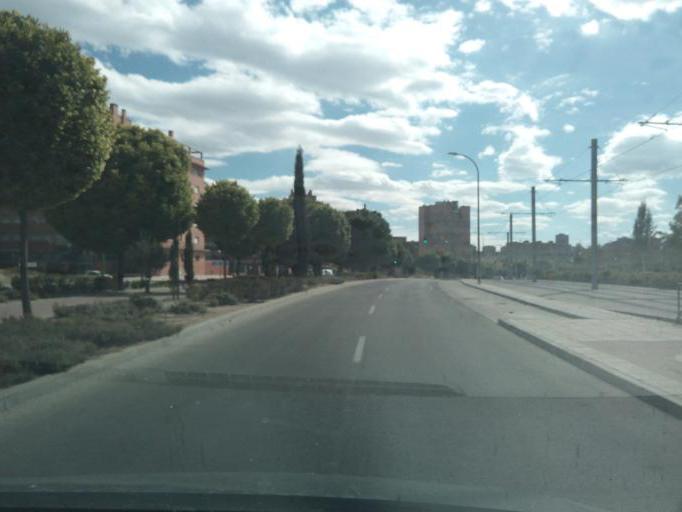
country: ES
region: Madrid
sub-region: Provincia de Madrid
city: Hortaleza
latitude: 40.4867
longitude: -3.6518
